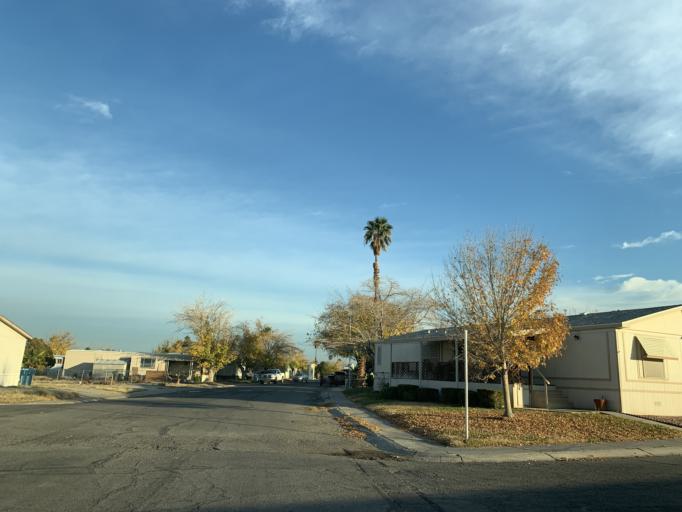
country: US
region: Nevada
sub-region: Clark County
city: Spring Valley
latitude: 36.1016
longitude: -115.2228
